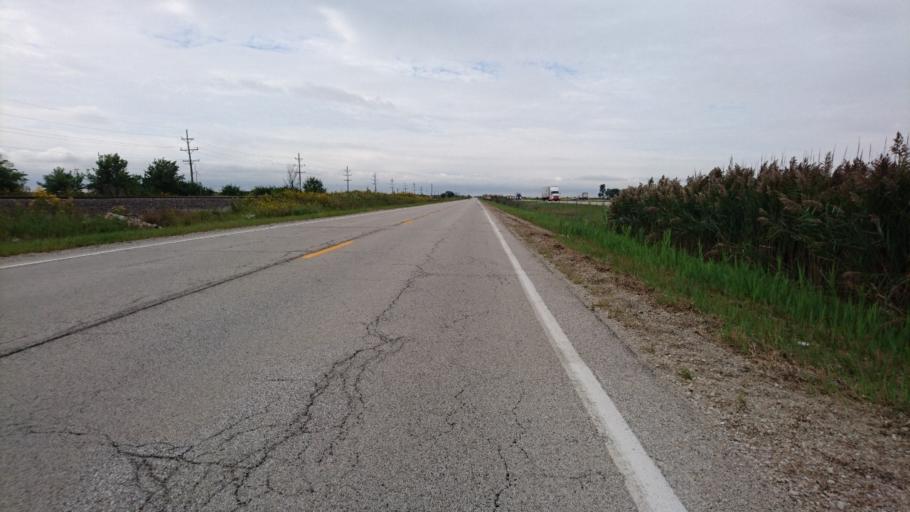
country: US
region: Illinois
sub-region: Livingston County
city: Odell
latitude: 41.0387
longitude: -88.4922
